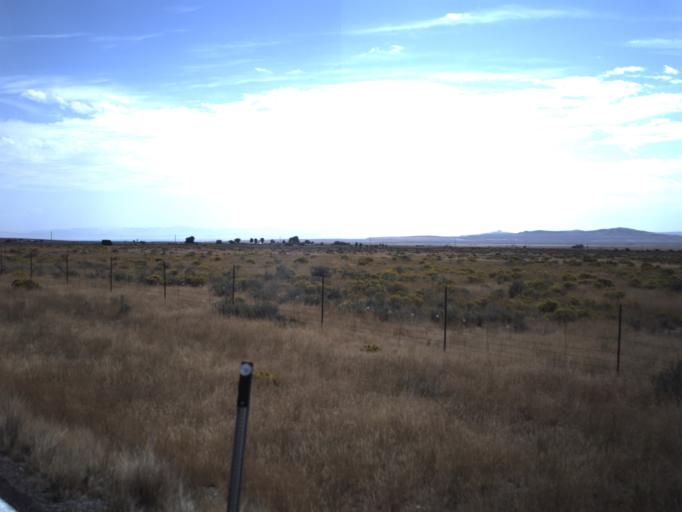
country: US
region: Idaho
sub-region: Cassia County
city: Burley
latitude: 41.8165
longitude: -113.3706
